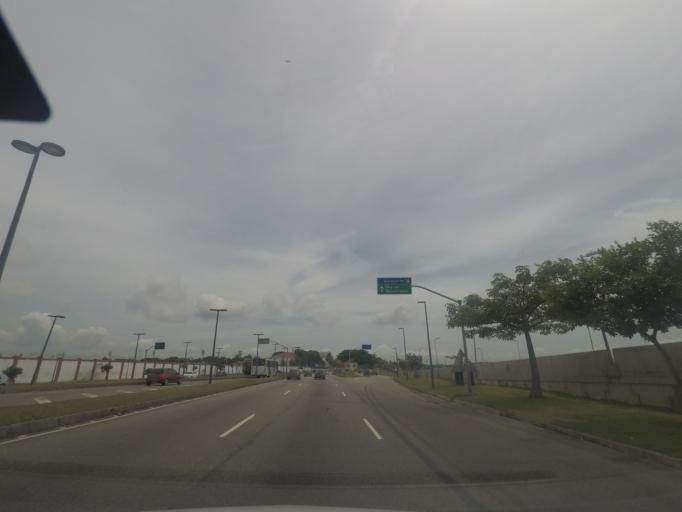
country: BR
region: Rio de Janeiro
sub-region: Rio De Janeiro
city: Rio de Janeiro
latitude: -22.8309
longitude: -43.2367
